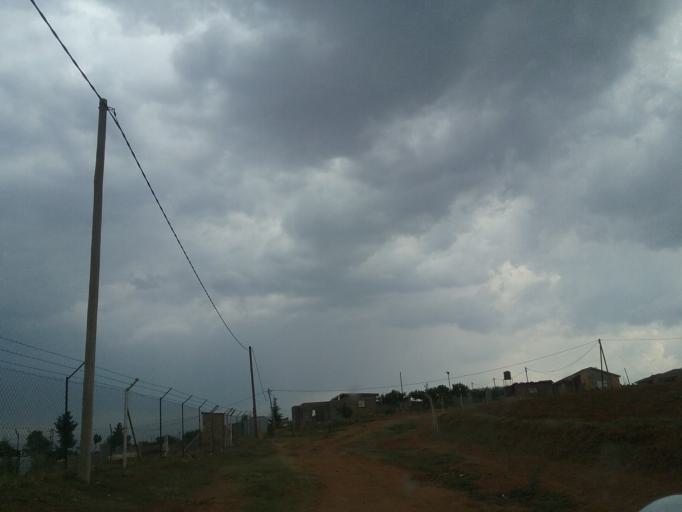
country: LS
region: Maseru
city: Maseru
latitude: -29.4192
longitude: 27.5678
